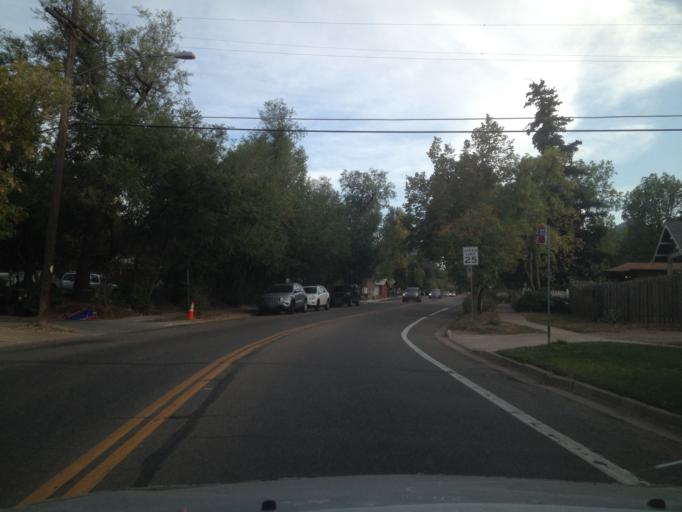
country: US
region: Colorado
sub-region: Boulder County
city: Boulder
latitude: 40.0101
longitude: -105.2821
